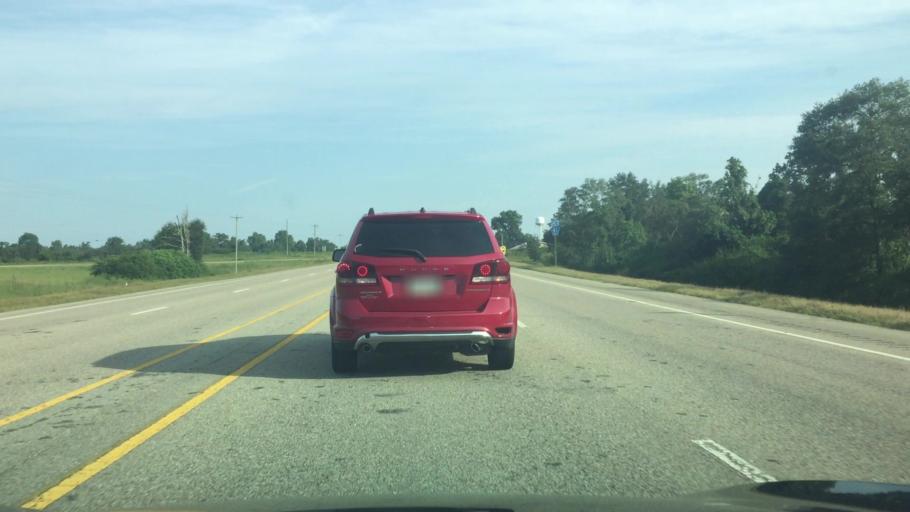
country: US
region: Alabama
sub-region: Butler County
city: Georgiana
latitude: 31.5243
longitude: -86.7163
